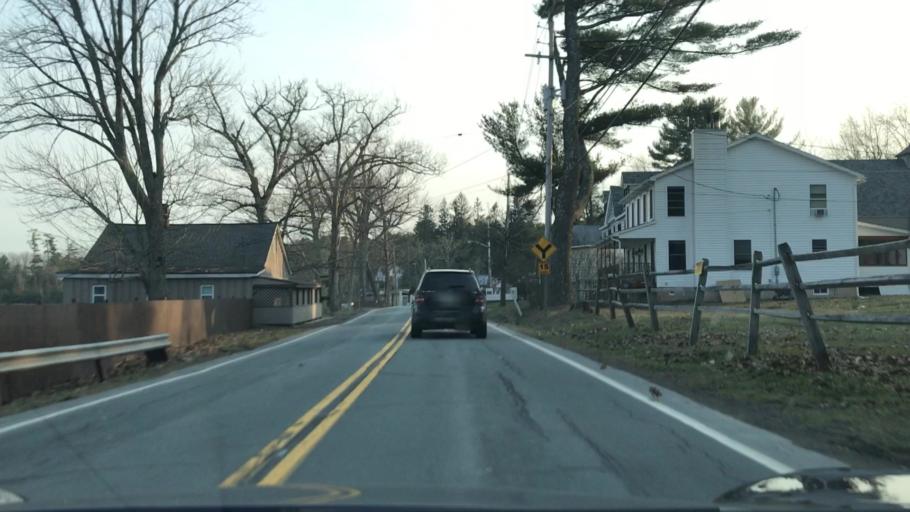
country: US
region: New York
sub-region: Sullivan County
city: Livingston Manor
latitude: 41.6838
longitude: -74.9930
